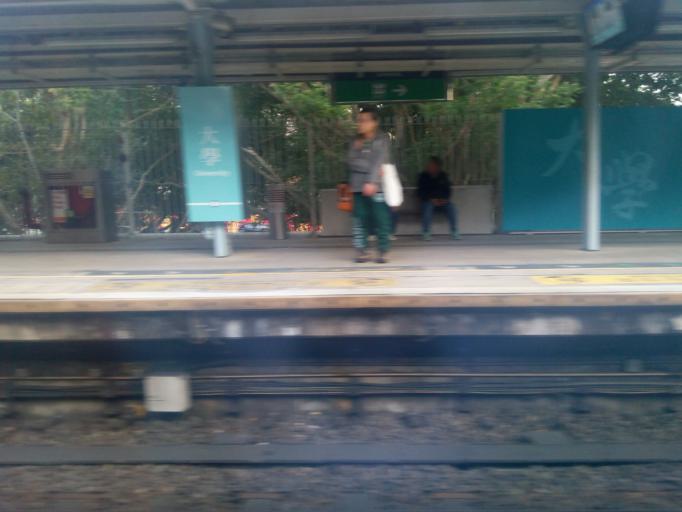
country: HK
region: Sha Tin
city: Sha Tin
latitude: 22.4139
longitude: 114.2102
